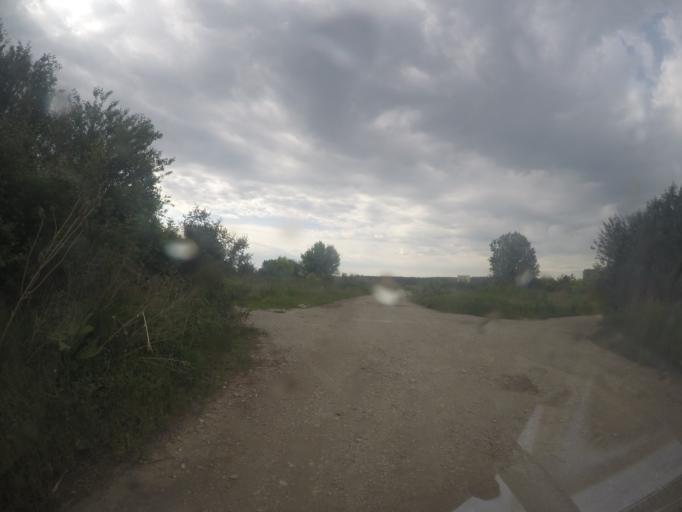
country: RS
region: Central Serbia
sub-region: Belgrade
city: Zemun
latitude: 44.8805
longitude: 20.3835
